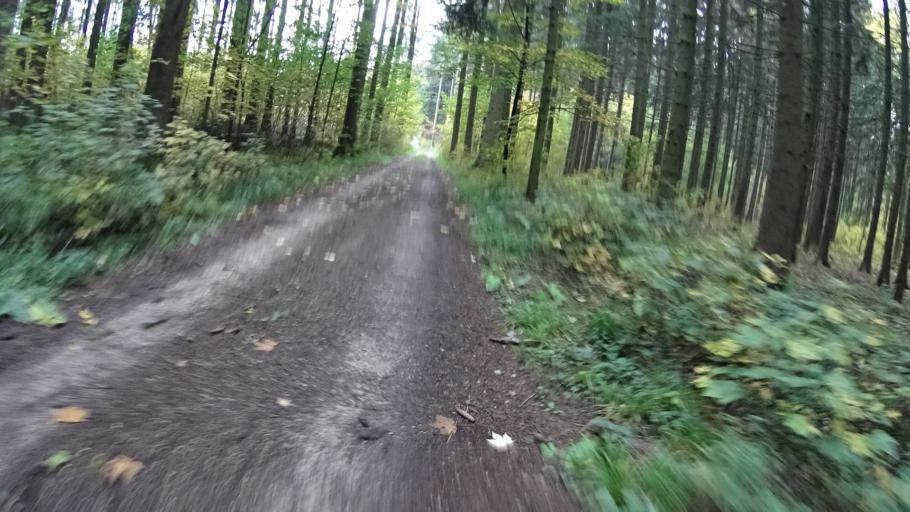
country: DE
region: Bavaria
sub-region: Upper Bavaria
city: Hitzhofen
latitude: 48.8465
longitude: 11.3006
